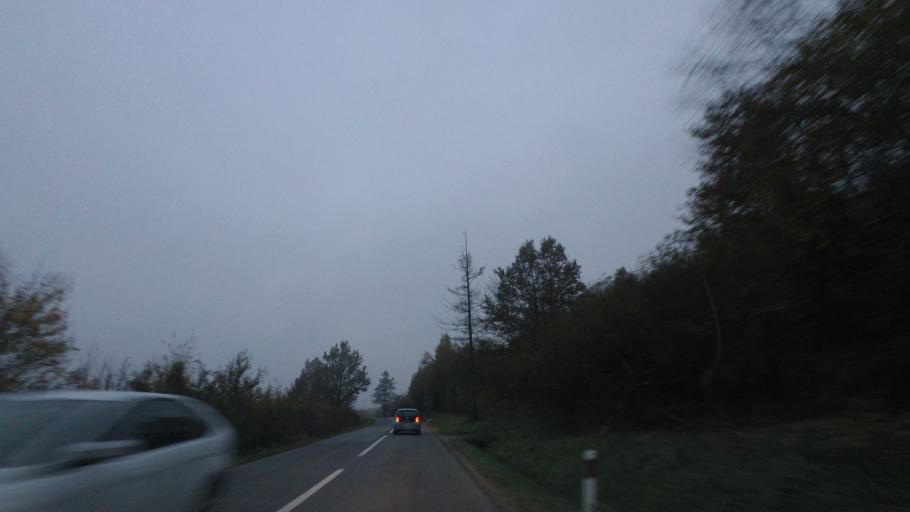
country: HR
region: Sisacko-Moslavacka
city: Glina
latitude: 45.4018
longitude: 16.1700
